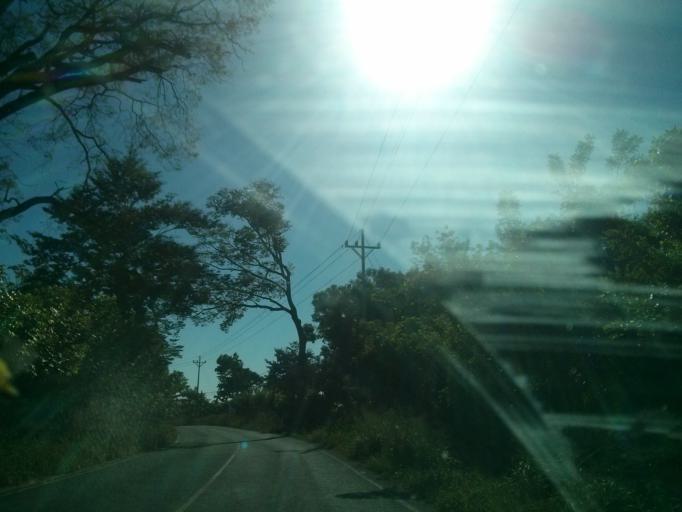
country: CR
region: Puntarenas
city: Paquera
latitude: 9.6986
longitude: -85.0760
